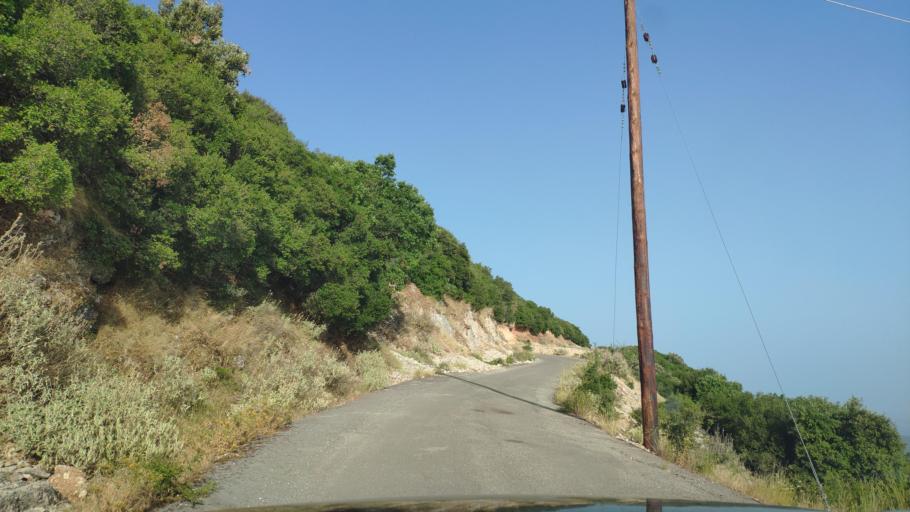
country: GR
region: West Greece
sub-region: Nomos Aitolias kai Akarnanias
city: Monastirakion
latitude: 38.8423
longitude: 20.9766
